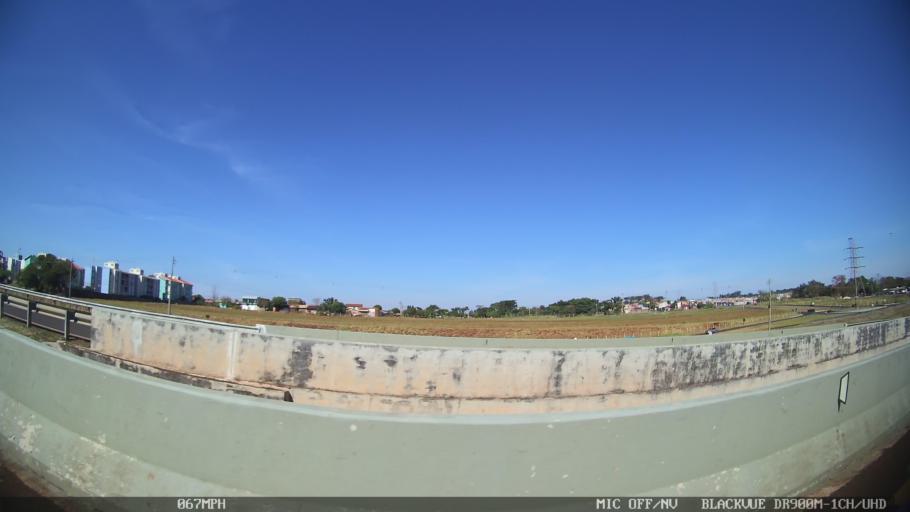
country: BR
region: Sao Paulo
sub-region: Ribeirao Preto
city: Ribeirao Preto
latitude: -21.1339
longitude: -47.8570
